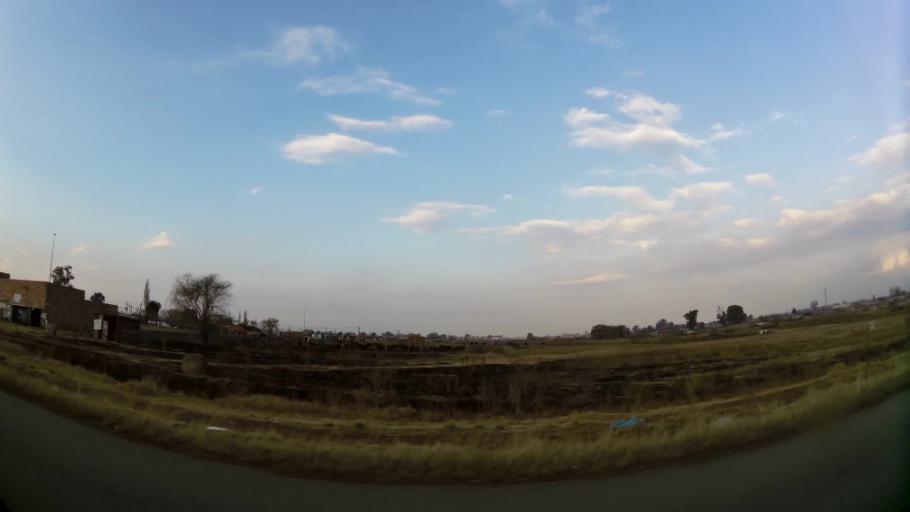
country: ZA
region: Gauteng
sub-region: City of Johannesburg Metropolitan Municipality
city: Orange Farm
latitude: -26.5425
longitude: 27.8327
